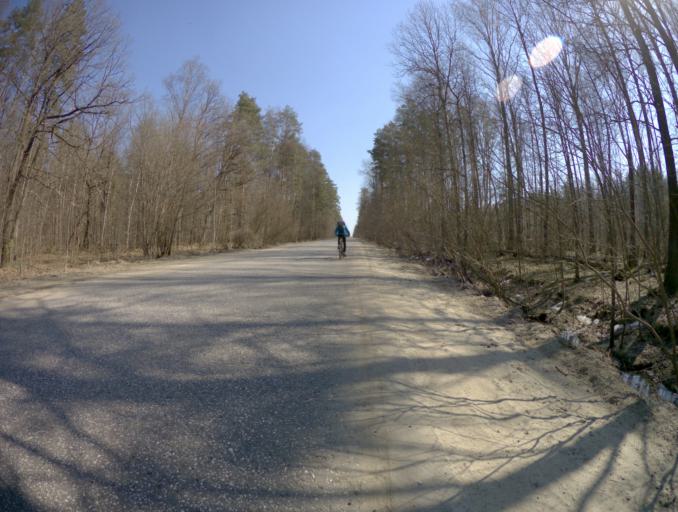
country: RU
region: Vladimir
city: Orgtrud
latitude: 56.1530
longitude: 40.5664
